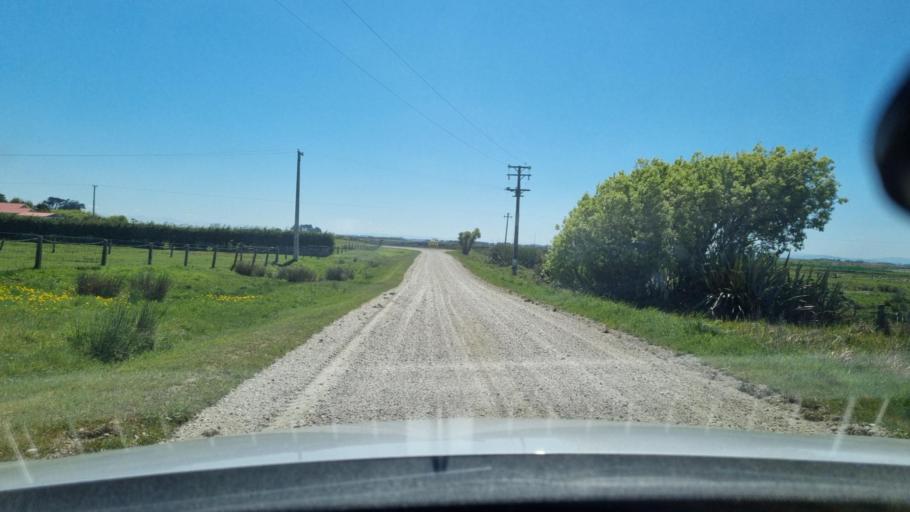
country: NZ
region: Southland
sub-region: Invercargill City
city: Invercargill
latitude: -46.4107
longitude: 168.2634
